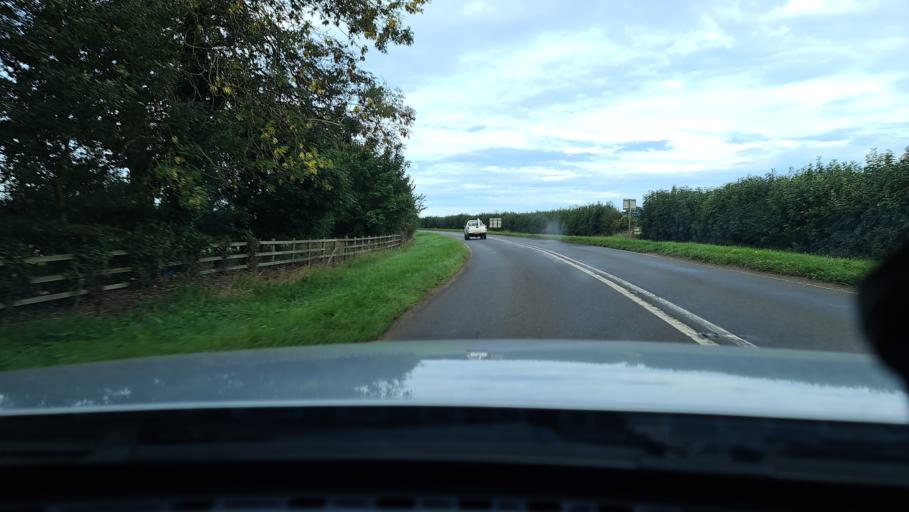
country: GB
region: England
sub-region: Oxfordshire
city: Hanwell
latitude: 52.1123
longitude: -1.4605
